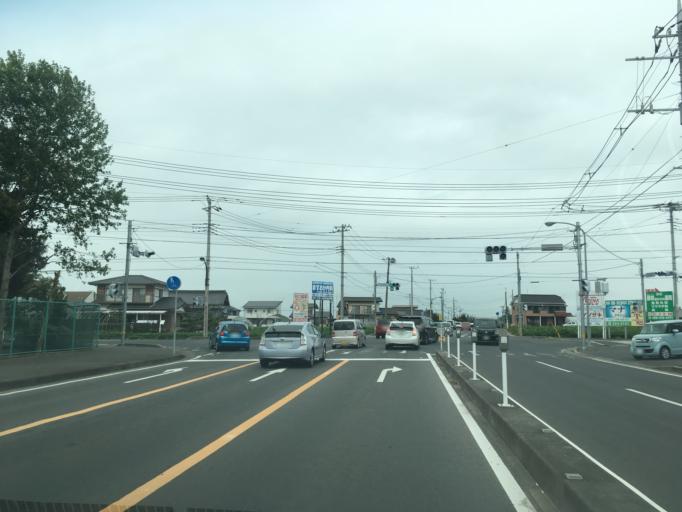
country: JP
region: Ibaraki
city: Hitachi-Naka
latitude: 36.4018
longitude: 140.5534
